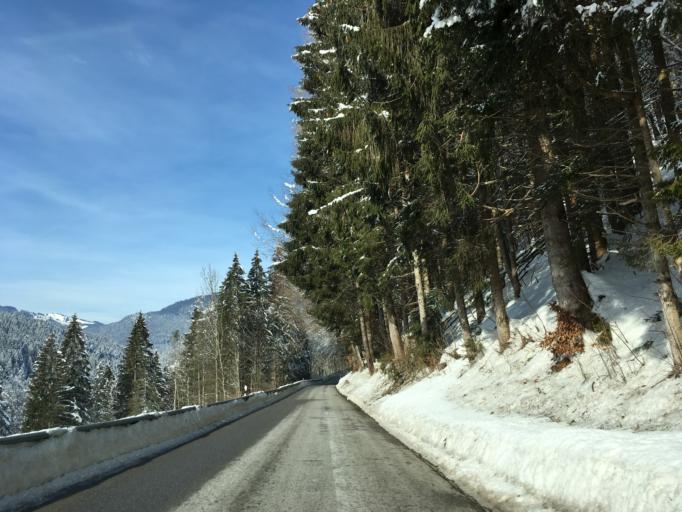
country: DE
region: Bavaria
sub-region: Upper Bavaria
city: Burg Unter-Falkenstein
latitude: 47.6607
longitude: 12.1187
